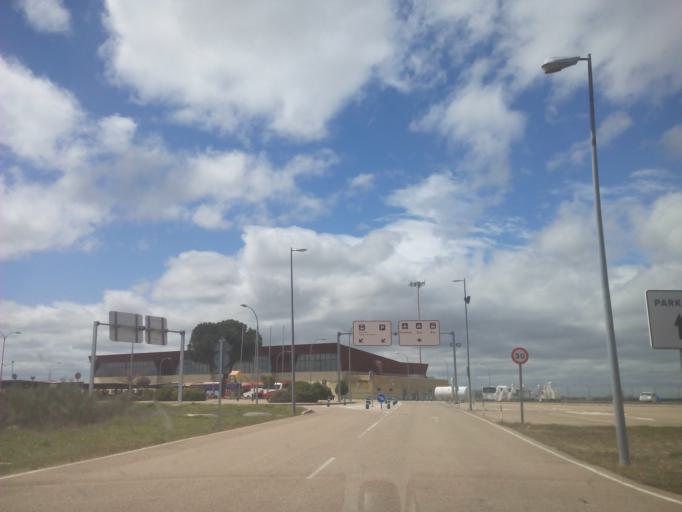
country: ES
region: Castille and Leon
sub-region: Provincia de Salamanca
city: Machacon
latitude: 40.9407
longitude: -5.5002
